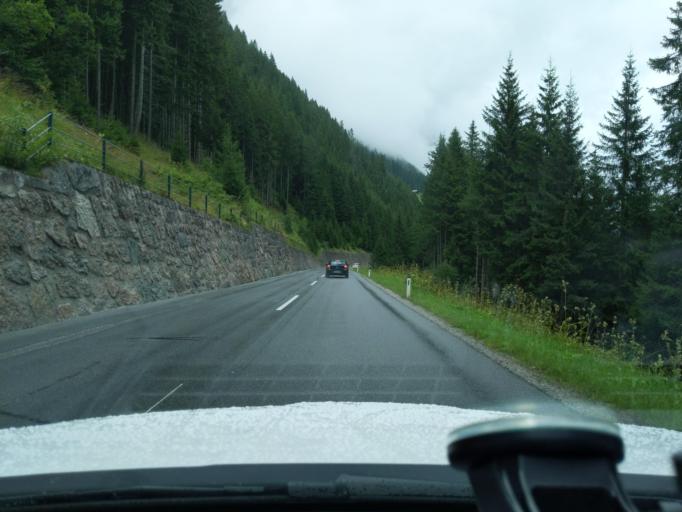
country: AT
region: Tyrol
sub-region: Politischer Bezirk Innsbruck Land
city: Schmirn
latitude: 47.1223
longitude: 11.6918
